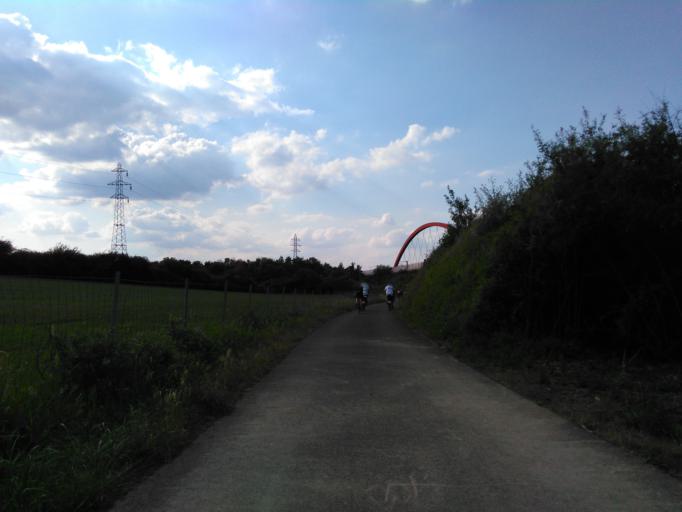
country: LU
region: Luxembourg
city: Bergem
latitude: 49.5084
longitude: 6.0359
